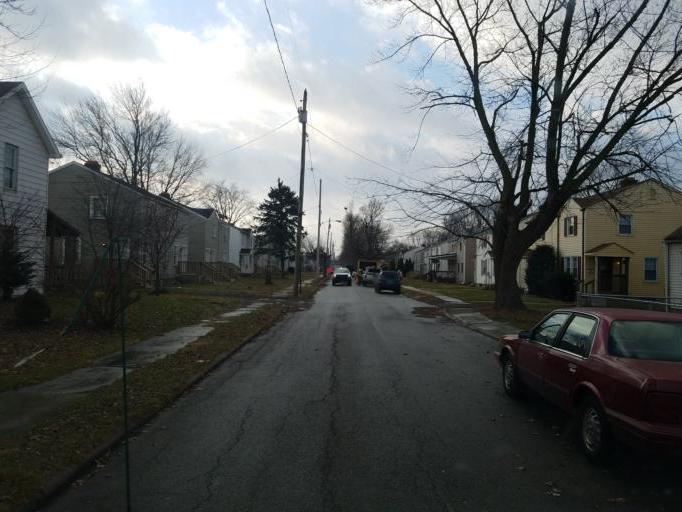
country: US
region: Ohio
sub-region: Marion County
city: Marion
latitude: 40.5995
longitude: -83.1349
